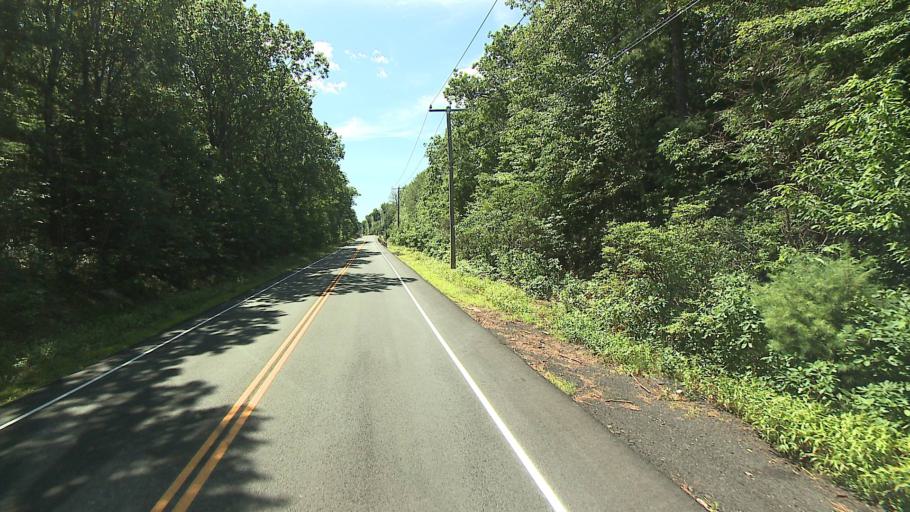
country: US
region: Connecticut
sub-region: Hartford County
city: North Granby
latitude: 41.9776
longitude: -72.9152
